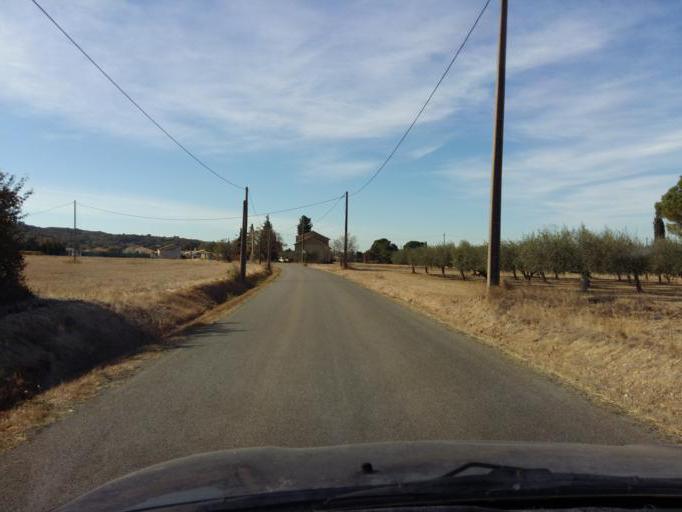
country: FR
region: Provence-Alpes-Cote d'Azur
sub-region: Departement du Vaucluse
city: Piolenc
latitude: 44.1810
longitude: 4.7810
